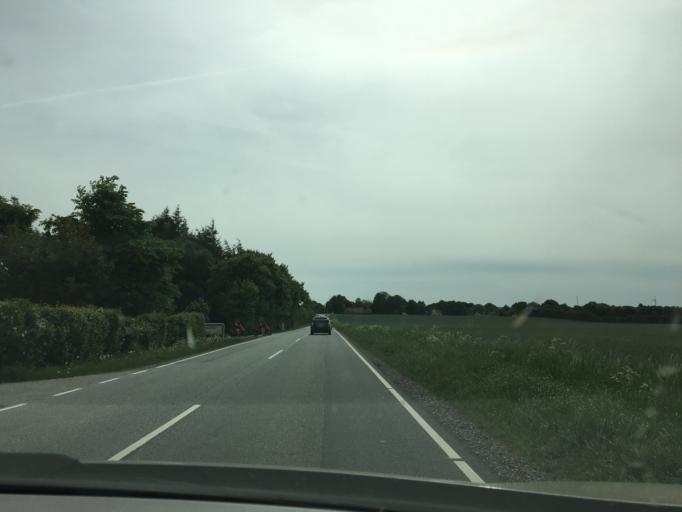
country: DK
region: Central Jutland
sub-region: Norddjurs Kommune
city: Allingabro
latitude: 56.4507
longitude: 10.2897
